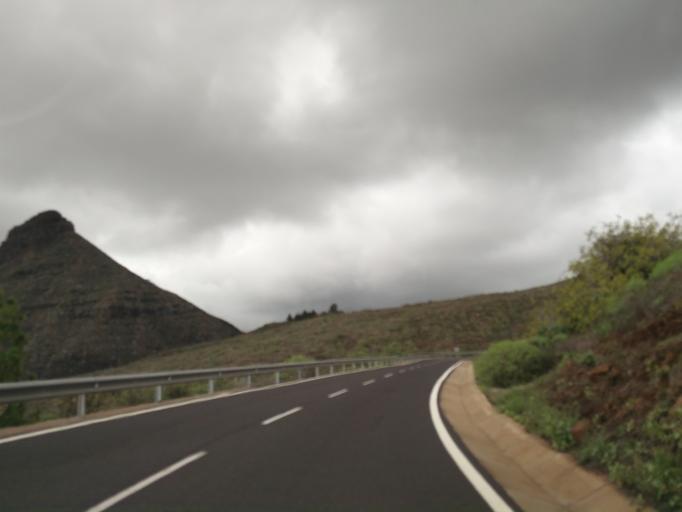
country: ES
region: Canary Islands
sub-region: Provincia de Santa Cruz de Tenerife
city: Arona
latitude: 28.1148
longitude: -16.6789
